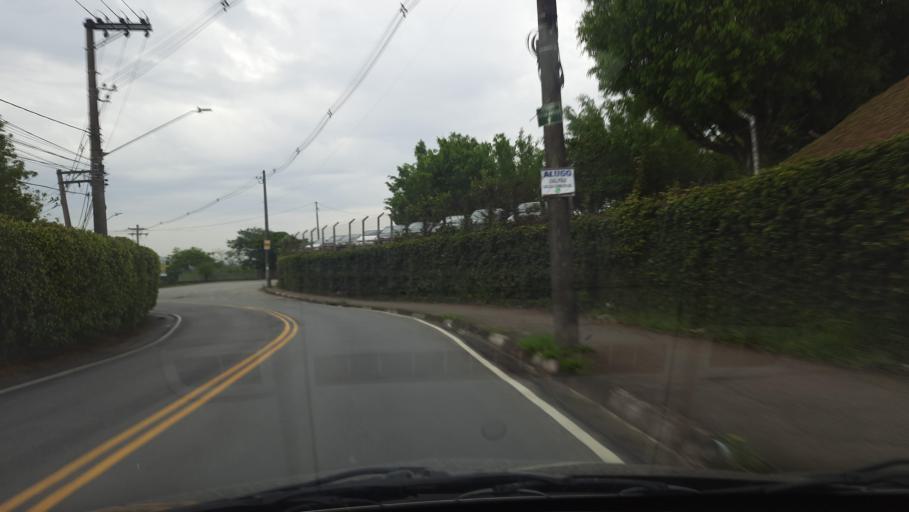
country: BR
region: Sao Paulo
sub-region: Caieiras
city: Caieiras
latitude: -23.3850
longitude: -46.7114
